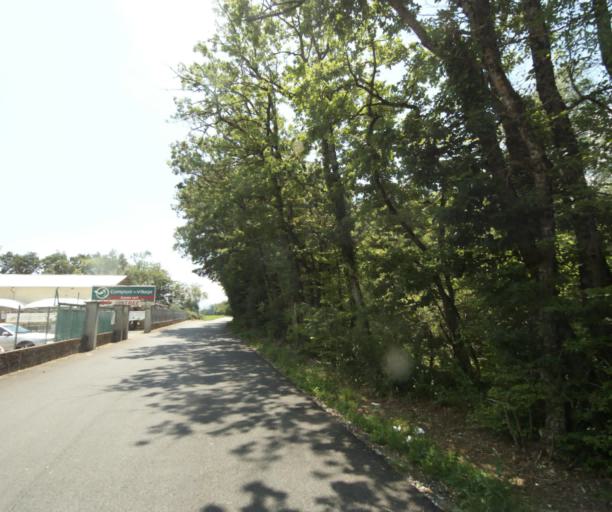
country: FR
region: Rhone-Alpes
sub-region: Departement de la Haute-Savoie
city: Douvaine
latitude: 46.3202
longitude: 6.2945
